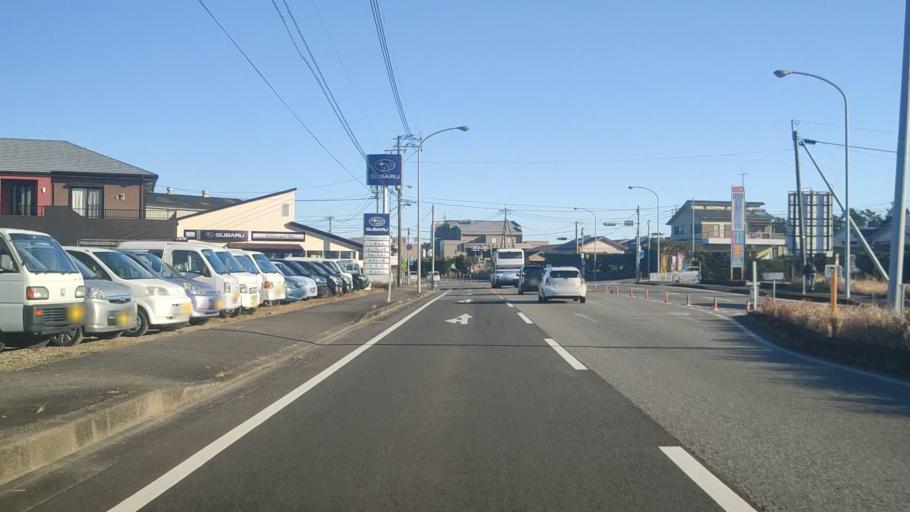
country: JP
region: Miyazaki
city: Nobeoka
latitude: 32.4611
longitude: 131.6479
